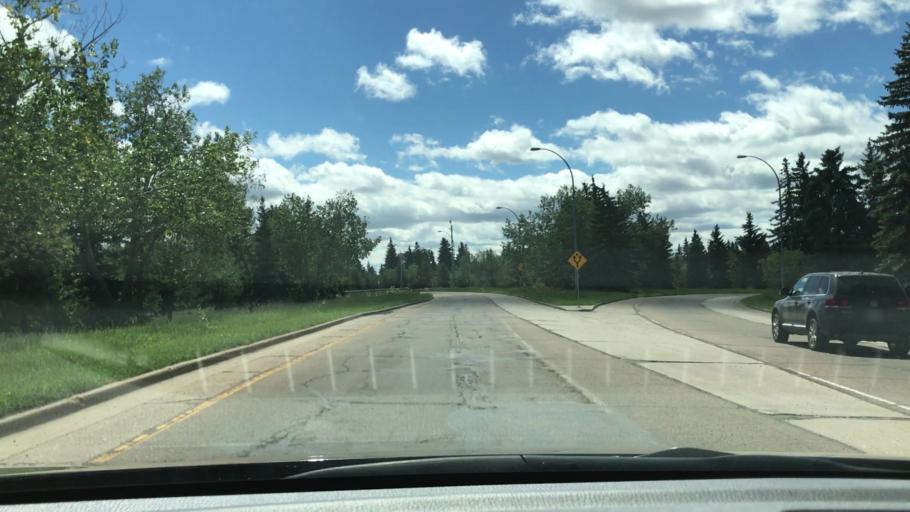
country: CA
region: Alberta
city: Edmonton
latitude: 53.5142
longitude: -113.5785
